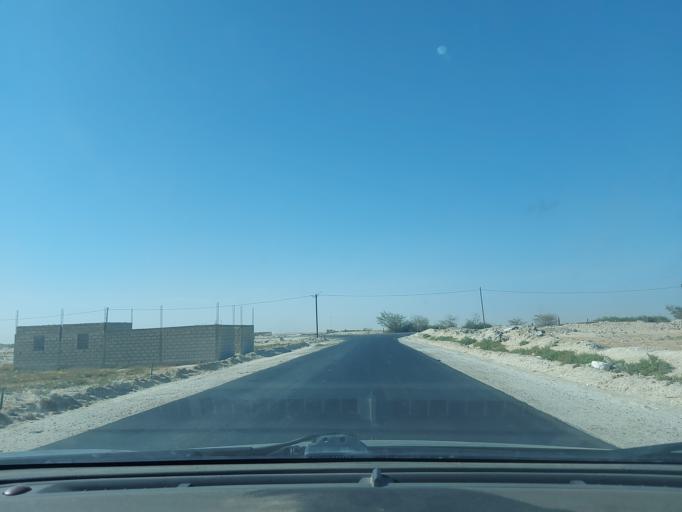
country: MR
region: Nouakchott
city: Nouakchott
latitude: 17.9933
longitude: -15.9882
